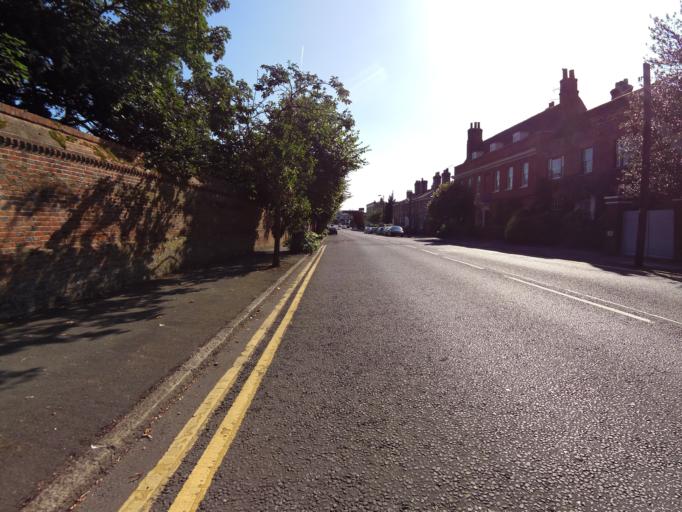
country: GB
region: England
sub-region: Essex
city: Witham
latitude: 51.8019
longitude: 0.6430
